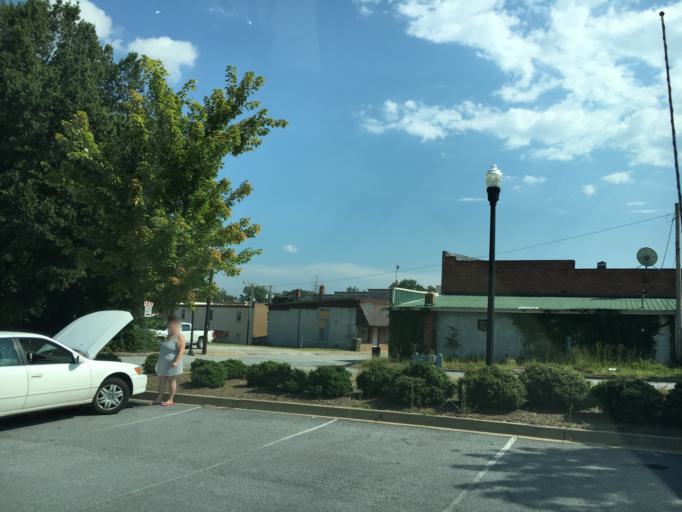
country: US
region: South Carolina
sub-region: Laurens County
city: Clinton
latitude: 34.4750
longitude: -81.8802
